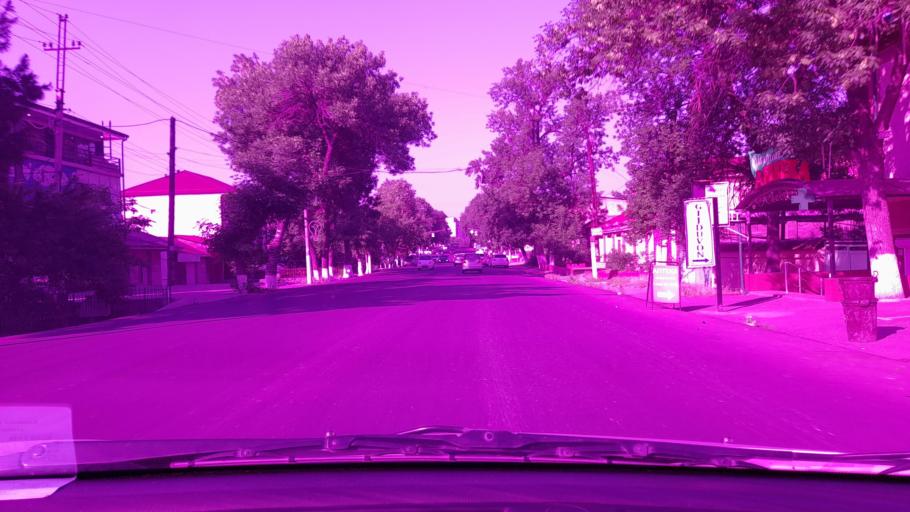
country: UZ
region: Toshkent
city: Salor
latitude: 41.3172
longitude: 69.3384
